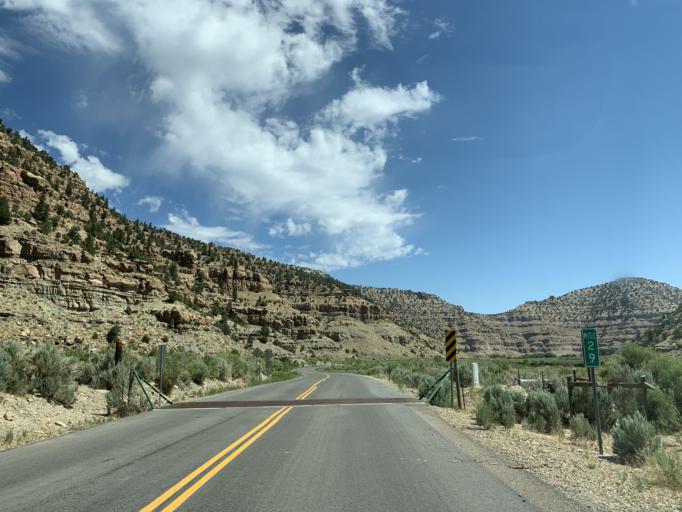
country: US
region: Utah
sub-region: Carbon County
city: East Carbon City
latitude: 39.7924
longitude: -110.3923
